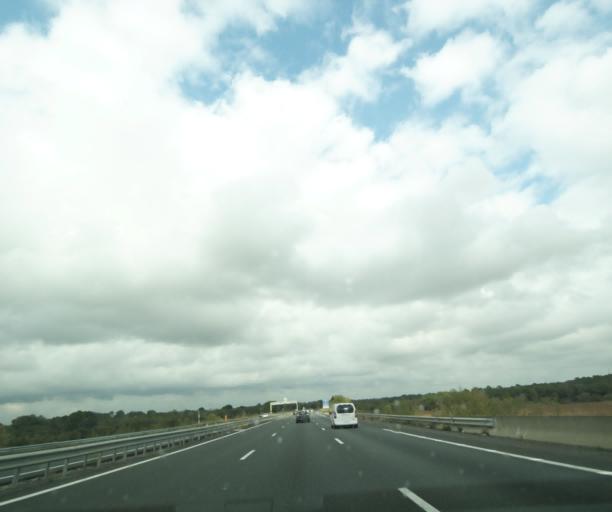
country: FR
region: Languedoc-Roussillon
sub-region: Departement de l'Herault
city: Cers
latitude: 43.3534
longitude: 3.3358
